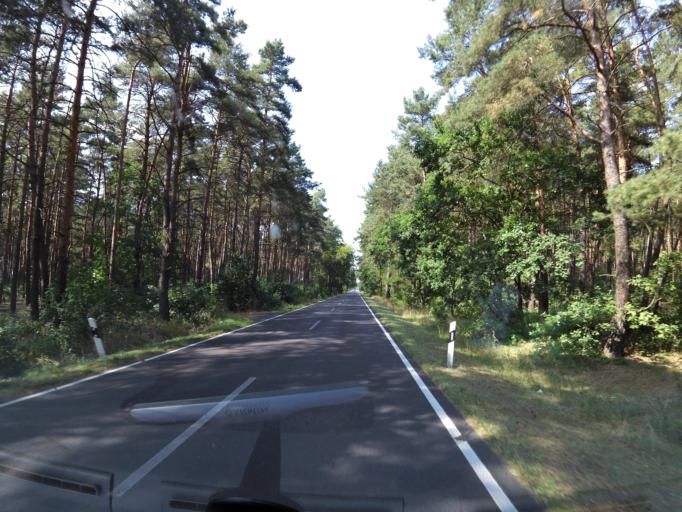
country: DE
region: Brandenburg
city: Zehdenick
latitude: 52.9581
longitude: 13.3743
